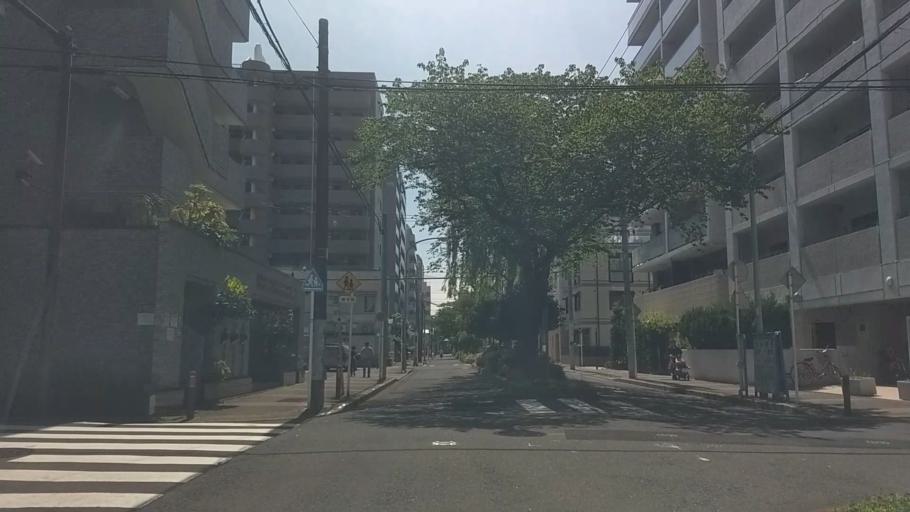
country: JP
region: Kanagawa
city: Yokohama
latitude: 35.4380
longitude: 139.6310
